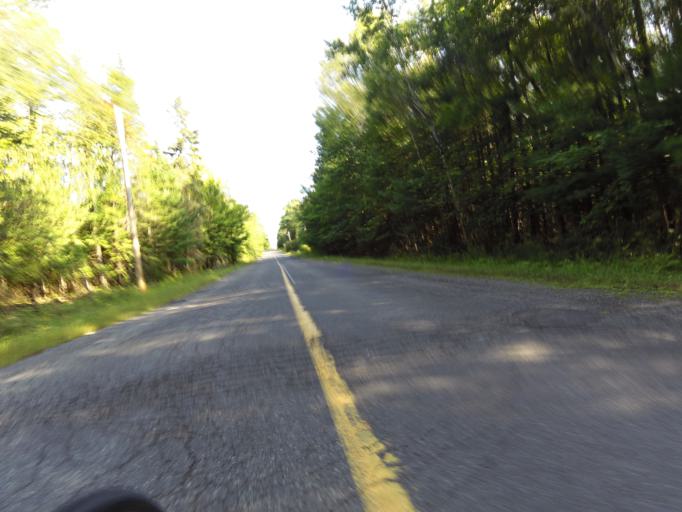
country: CA
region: Ontario
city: Bells Corners
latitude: 45.4772
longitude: -76.0214
